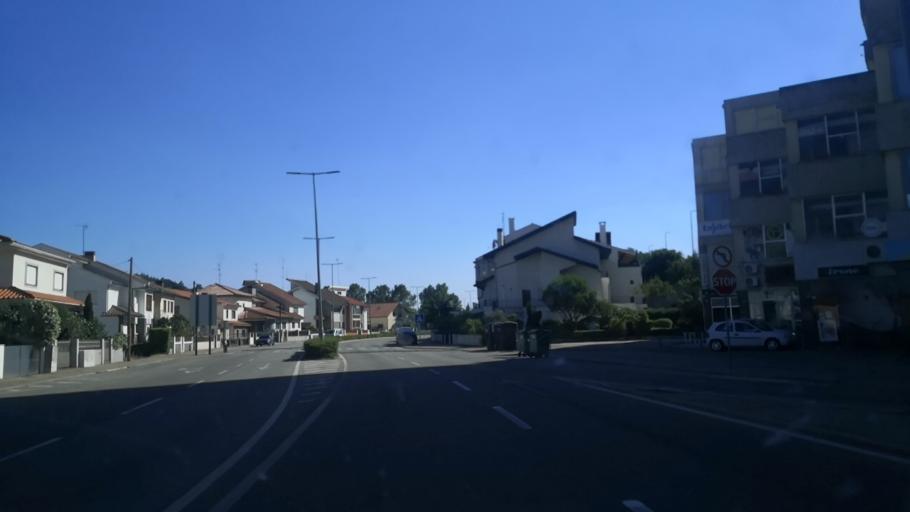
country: PT
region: Braganca
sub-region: Braganca Municipality
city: Braganca
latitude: 41.8009
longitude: -6.7637
